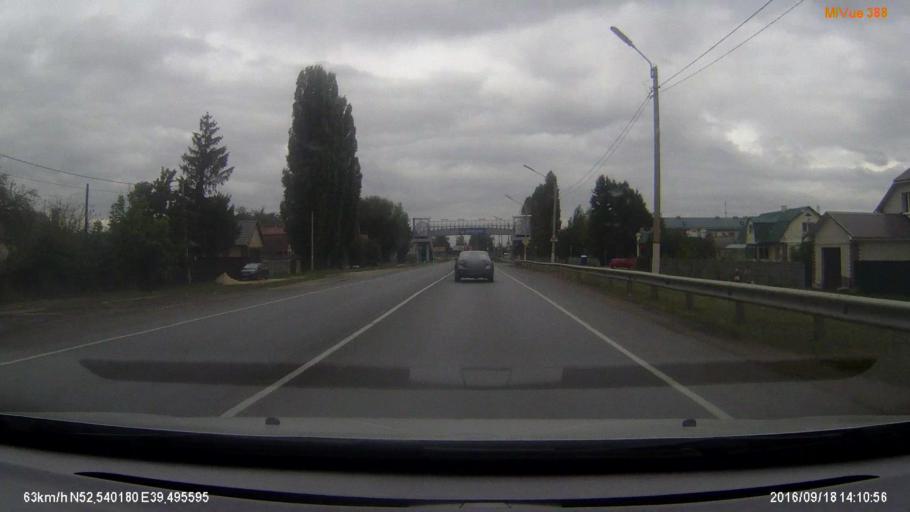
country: RU
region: Lipetsk
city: Syrskoye
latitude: 52.5918
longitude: 39.5154
